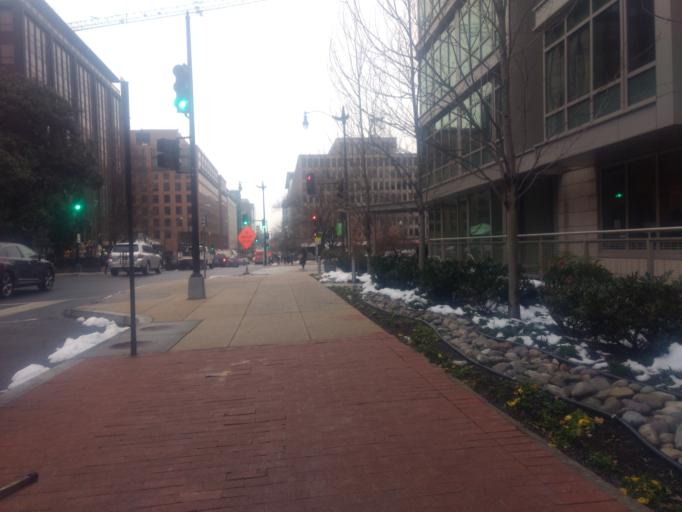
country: US
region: Washington, D.C.
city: Washington, D.C.
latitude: 38.9066
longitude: -77.0468
